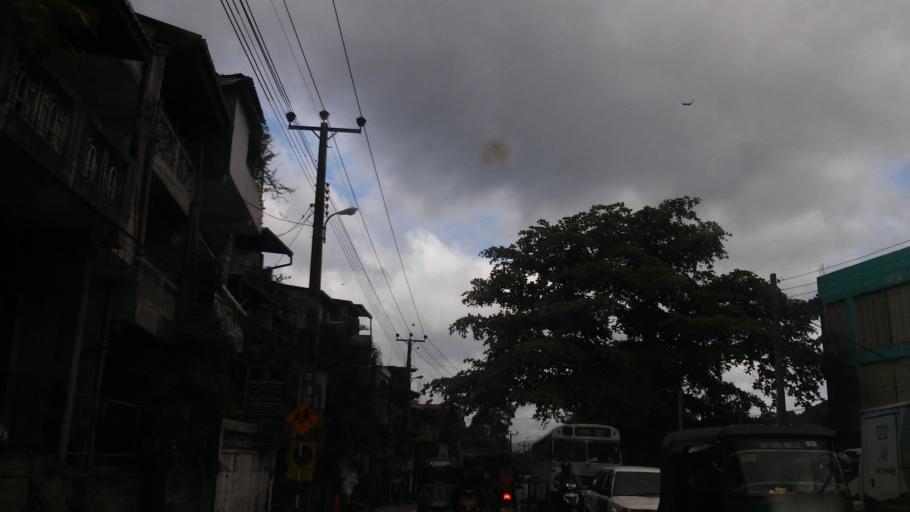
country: LK
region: Central
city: Kandy
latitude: 7.2873
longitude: 80.6306
